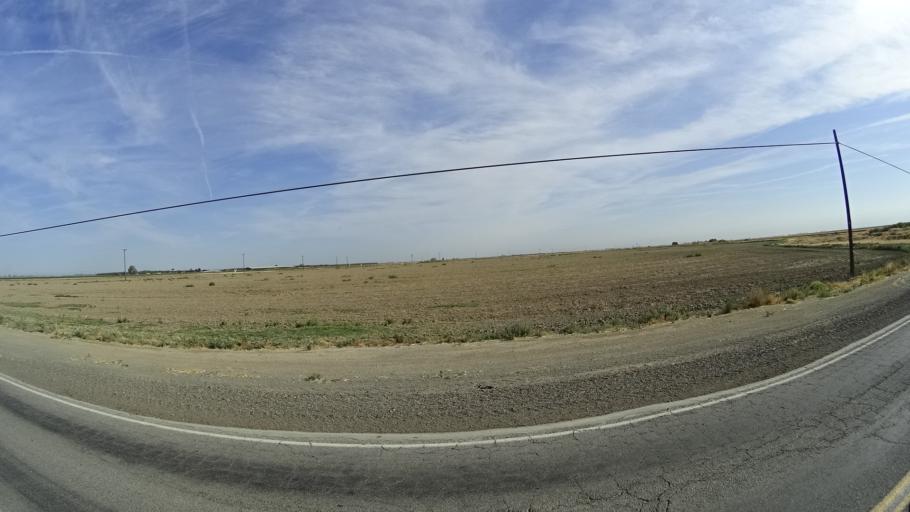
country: US
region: California
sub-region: Kings County
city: Home Garden
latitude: 36.3429
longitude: -119.5368
